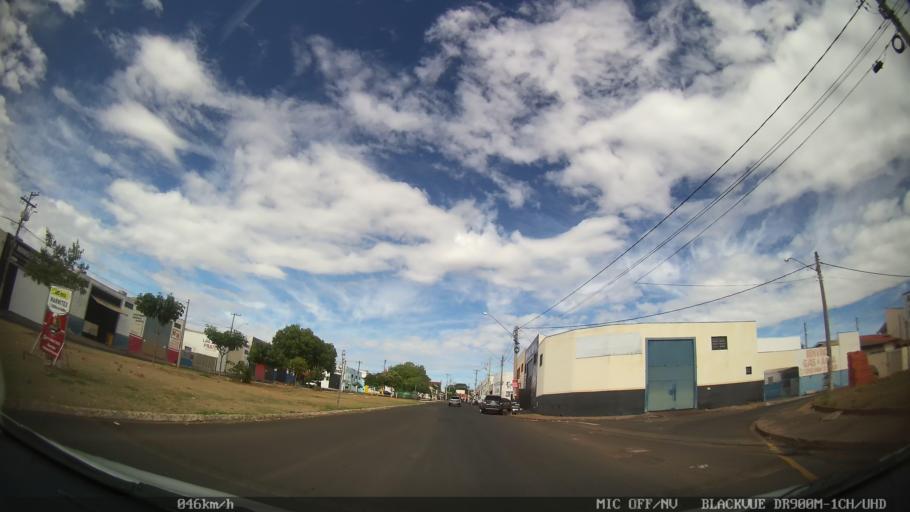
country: BR
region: Sao Paulo
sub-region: Sao Jose Do Rio Preto
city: Sao Jose do Rio Preto
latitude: -20.8042
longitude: -49.5054
